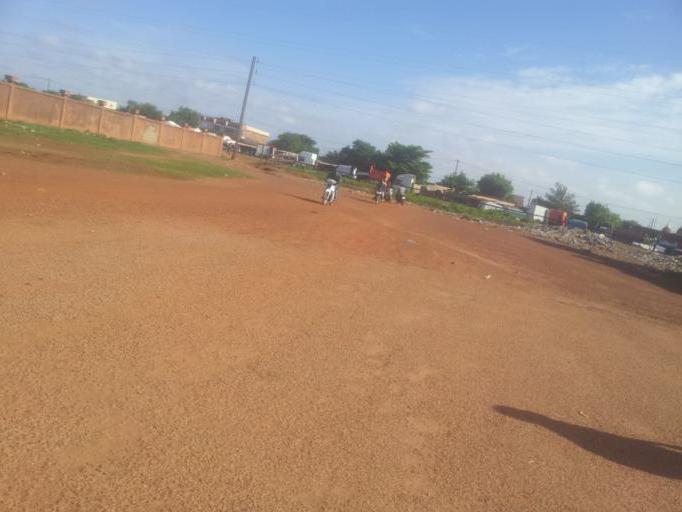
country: BF
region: Centre
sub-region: Kadiogo Province
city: Ouagadougou
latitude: 12.3696
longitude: -1.5554
